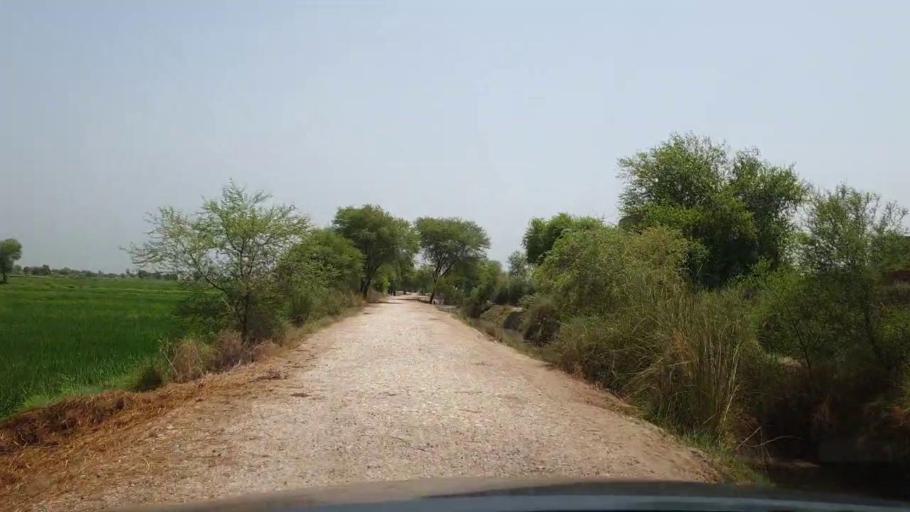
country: PK
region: Sindh
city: Madeji
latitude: 27.7776
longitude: 68.4013
